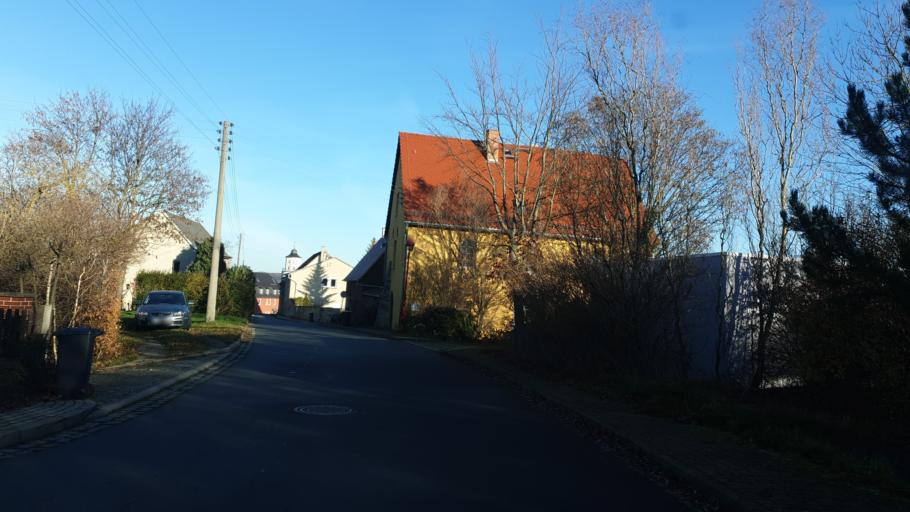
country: DE
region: Thuringia
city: Hartmannsdorf
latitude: 50.9768
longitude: 11.9717
